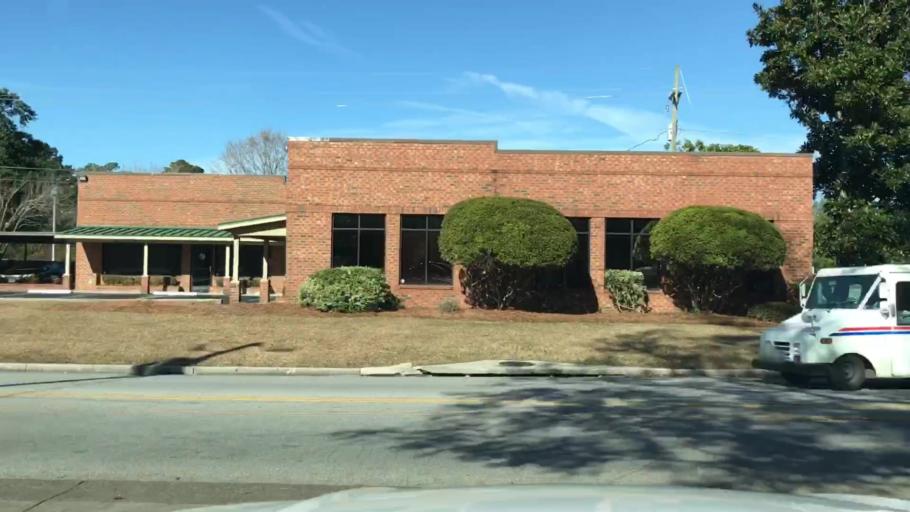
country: US
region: South Carolina
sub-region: Charleston County
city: North Charleston
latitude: 32.8065
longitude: -80.0236
